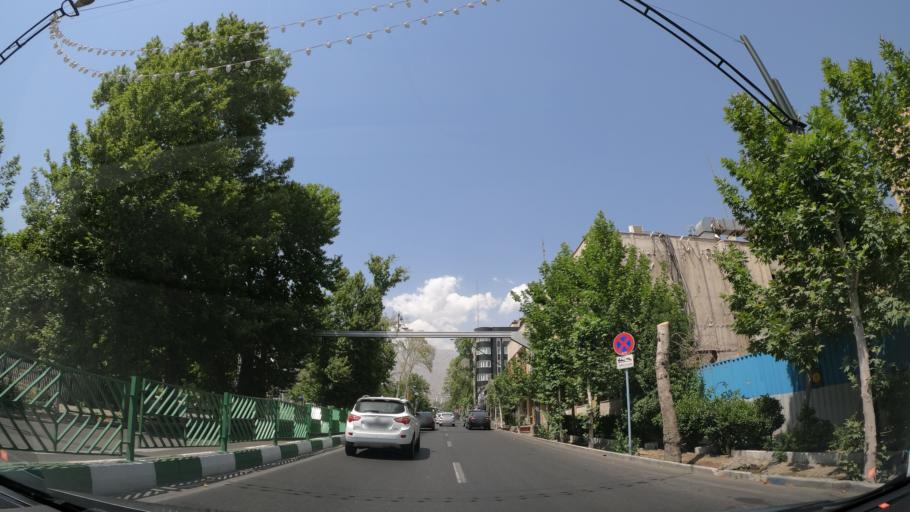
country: IR
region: Tehran
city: Tajrish
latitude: 35.7804
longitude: 51.4140
